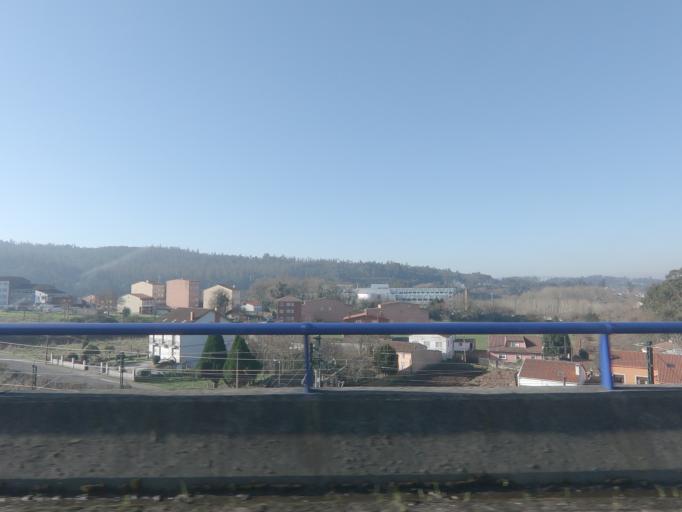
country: ES
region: Galicia
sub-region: Provincia da Coruna
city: Santiago de Compostela
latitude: 42.8619
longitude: -8.5485
